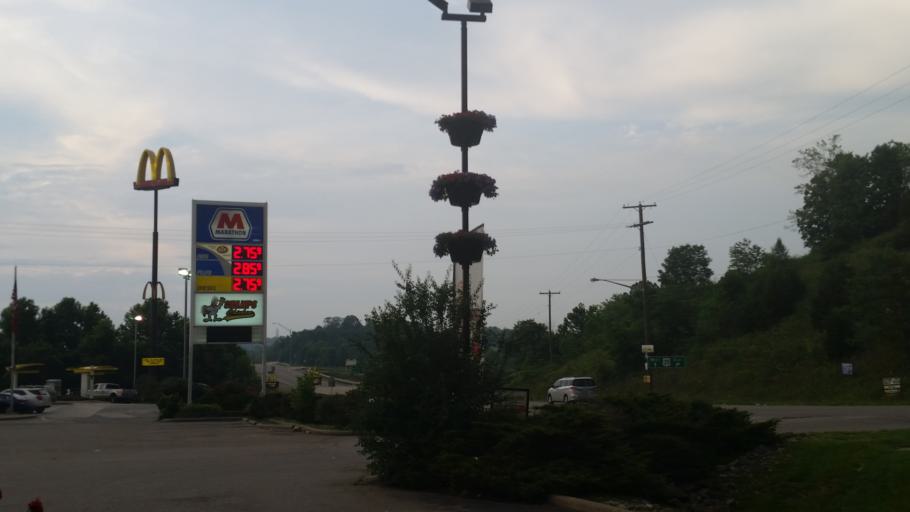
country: US
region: Ohio
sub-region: Jackson County
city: Oak Hill
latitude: 38.8877
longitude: -82.3823
